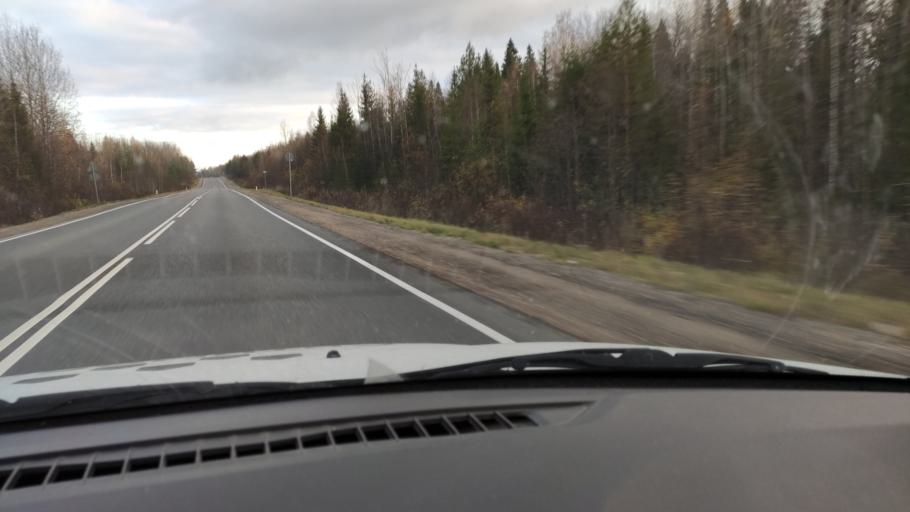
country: RU
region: Kirov
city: Omutninsk
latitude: 58.7072
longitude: 52.1026
